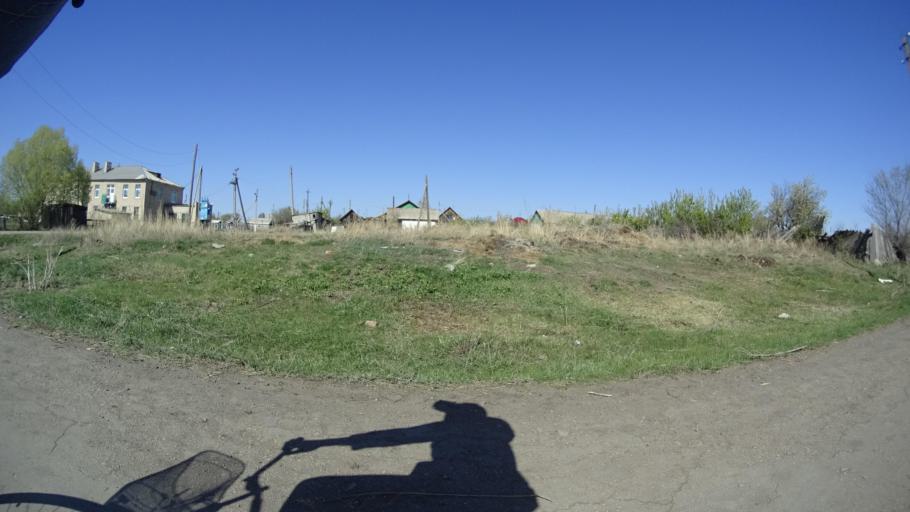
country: RU
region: Chelyabinsk
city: Chesma
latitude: 53.7948
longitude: 61.0299
